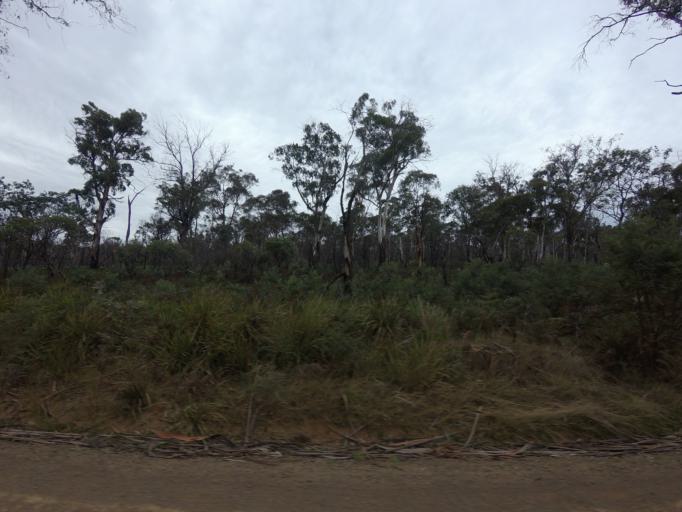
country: AU
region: Tasmania
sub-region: Derwent Valley
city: New Norfolk
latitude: -42.5545
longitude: 146.9610
